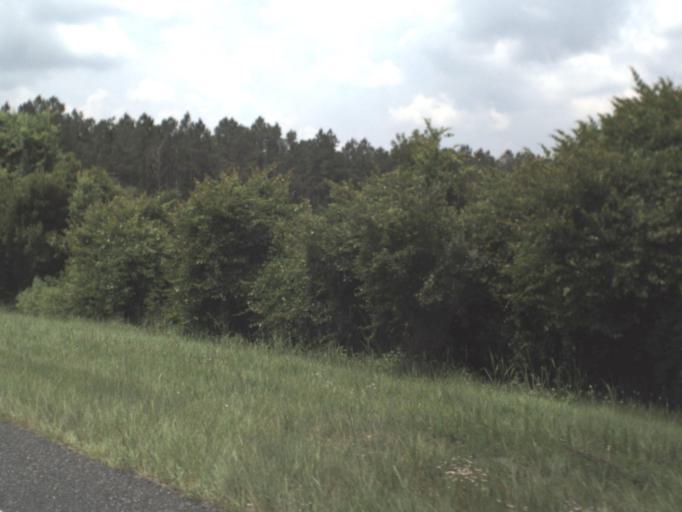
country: US
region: Florida
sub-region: Putnam County
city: East Palatka
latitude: 29.7678
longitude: -81.6389
